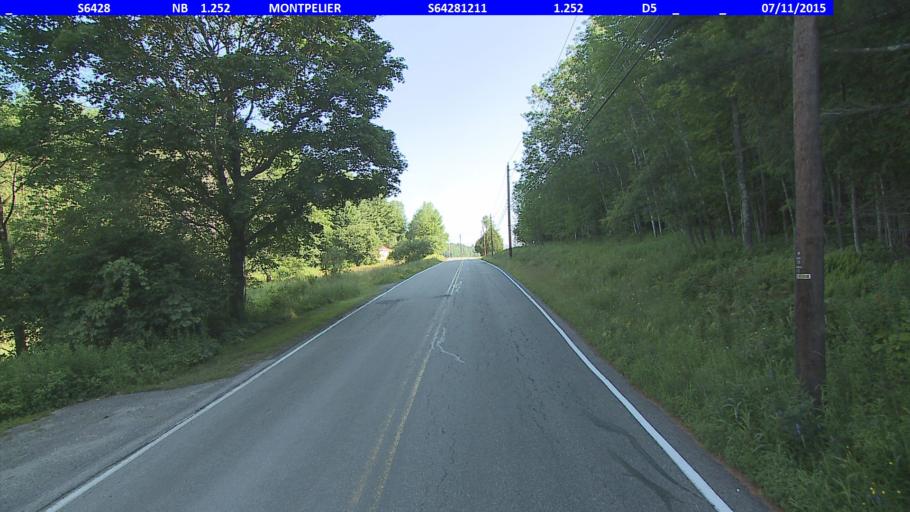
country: US
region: Vermont
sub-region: Washington County
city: Montpelier
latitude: 44.2792
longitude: -72.5935
